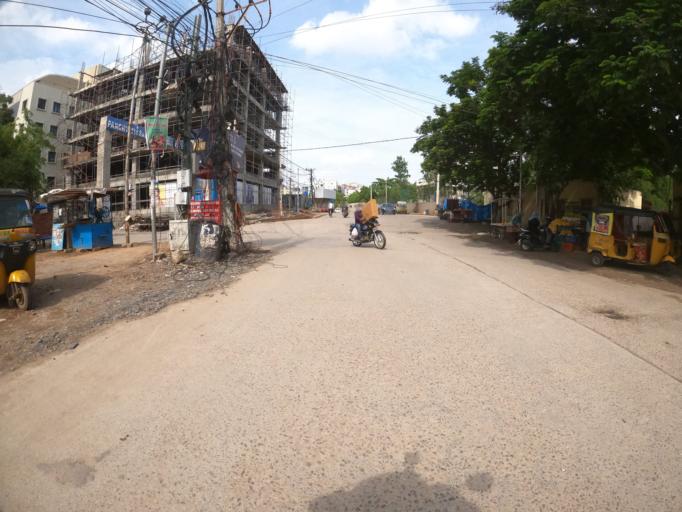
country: IN
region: Telangana
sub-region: Hyderabad
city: Hyderabad
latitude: 17.4070
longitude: 78.3843
